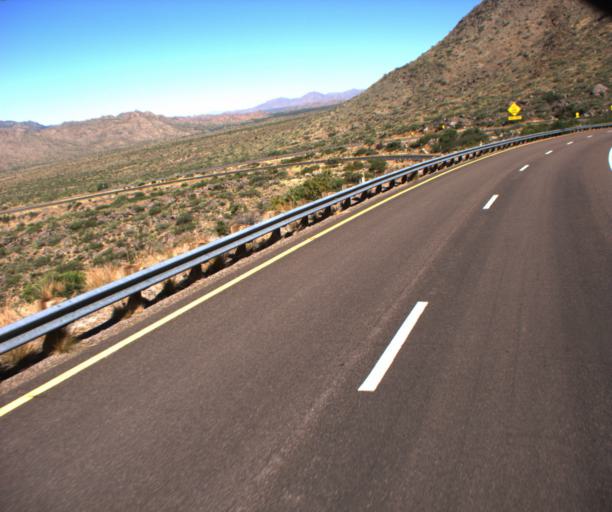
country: US
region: Arizona
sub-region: Yavapai County
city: Congress
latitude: 34.2063
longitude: -112.7980
